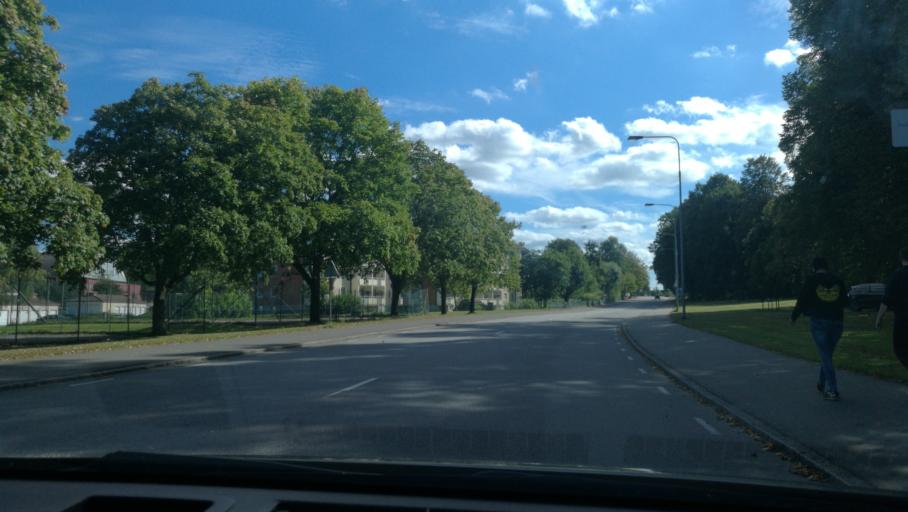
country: SE
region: Vaestra Goetaland
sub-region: Mariestads Kommun
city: Mariestad
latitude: 58.7052
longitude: 13.8326
